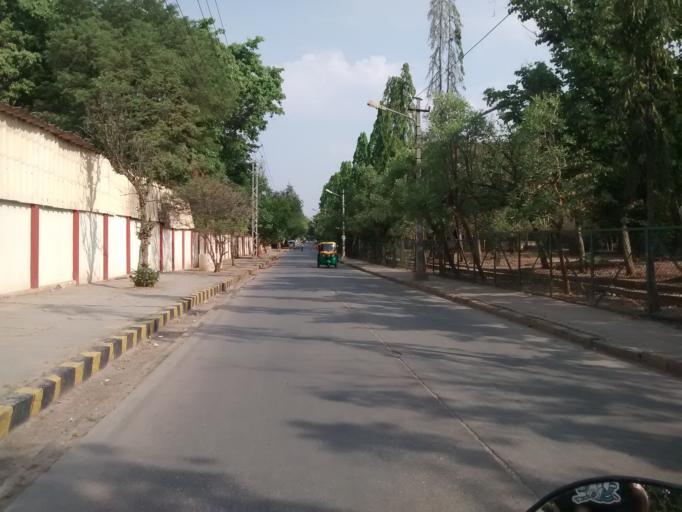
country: IN
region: Karnataka
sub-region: Bangalore Urban
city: Bangalore
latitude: 12.9650
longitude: 77.6632
